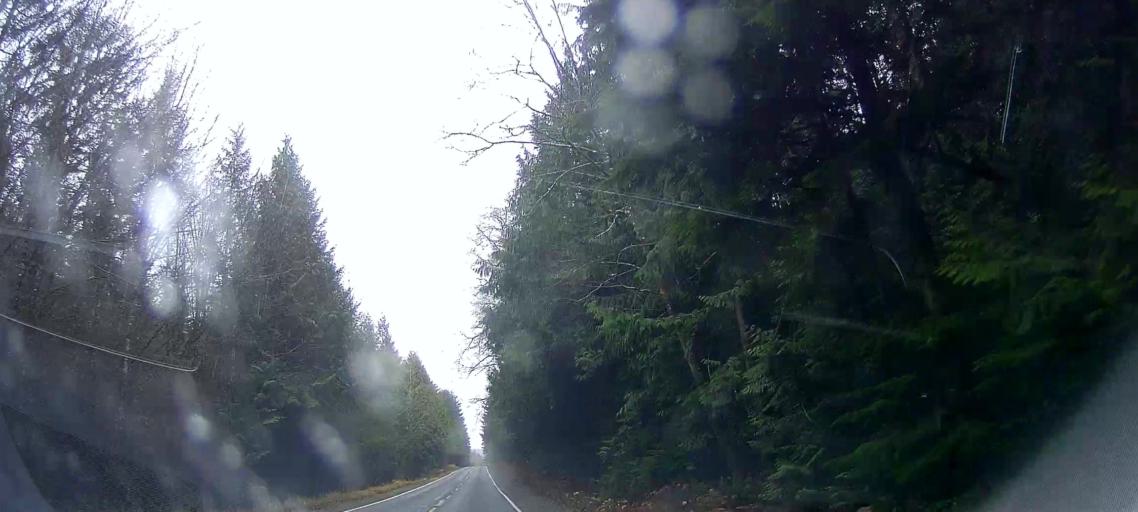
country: US
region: Washington
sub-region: Snohomish County
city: Darrington
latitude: 48.5312
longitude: -121.8040
